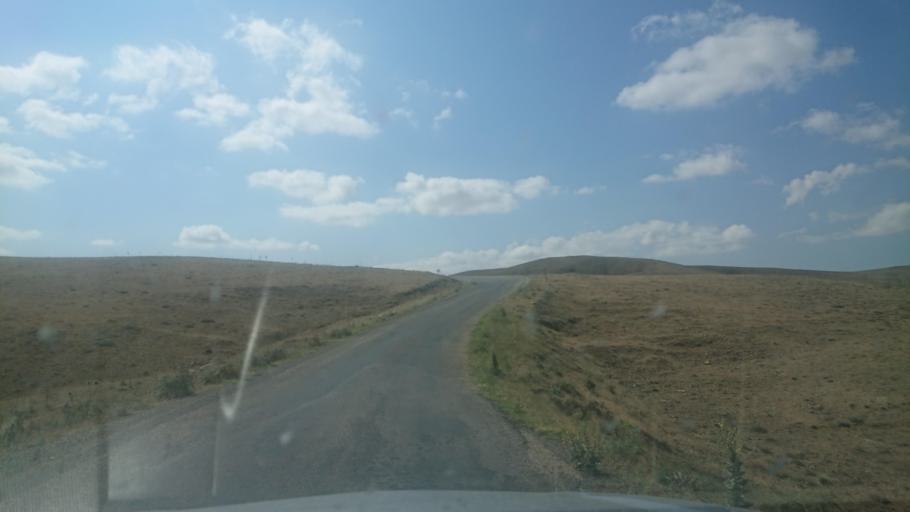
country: TR
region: Aksaray
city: Sariyahsi
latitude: 39.0065
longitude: 33.9569
